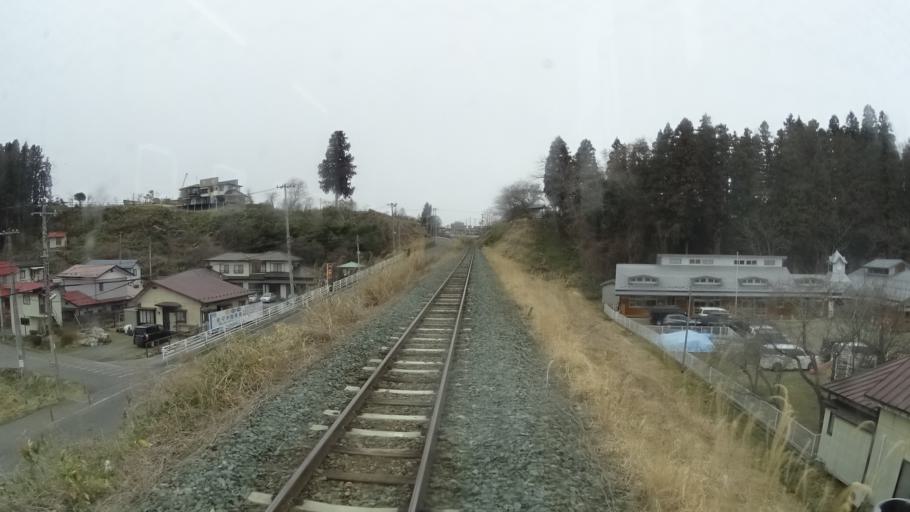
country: JP
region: Iwate
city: Hanamaki
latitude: 39.3878
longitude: 141.2256
